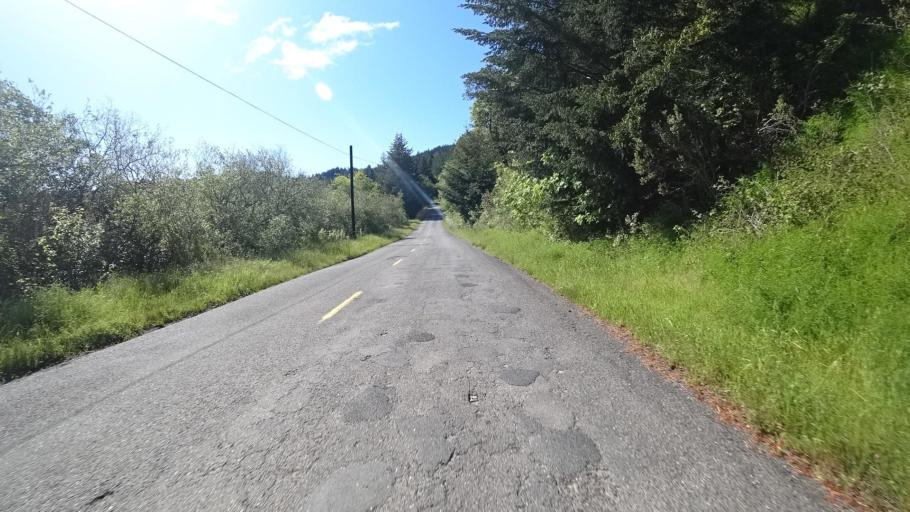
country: US
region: California
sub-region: Humboldt County
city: Rio Dell
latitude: 40.3083
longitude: -124.2593
